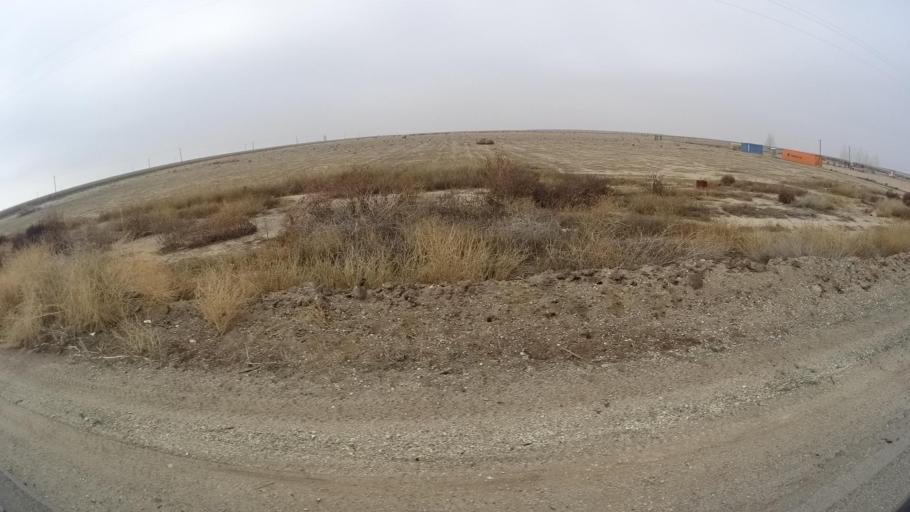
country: US
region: California
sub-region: Kern County
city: Maricopa
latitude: 35.0778
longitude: -119.3139
